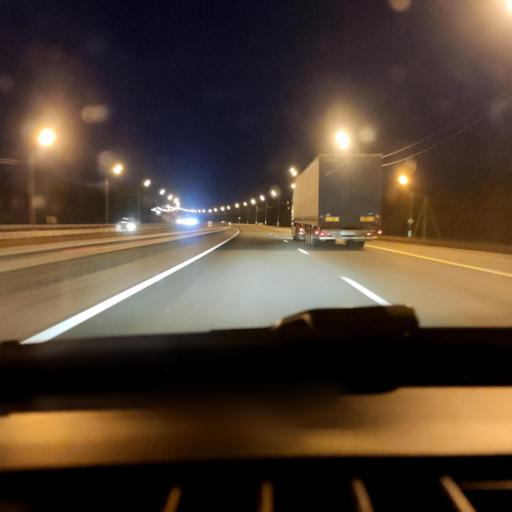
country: RU
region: Lipetsk
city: Khlevnoye
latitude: 52.0964
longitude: 39.1764
